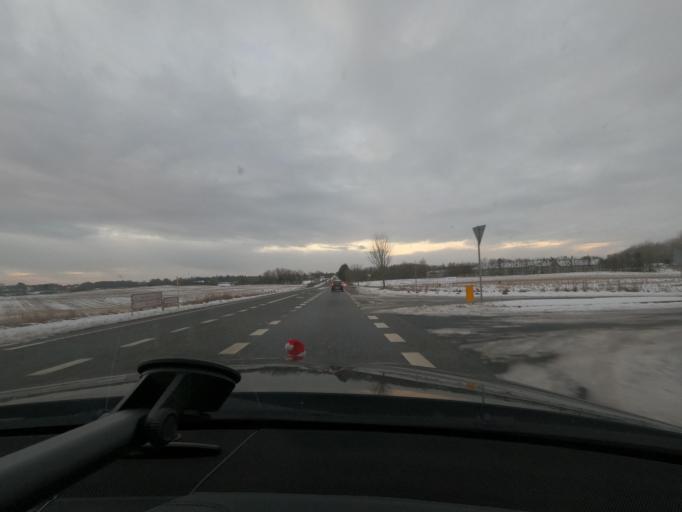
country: DK
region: South Denmark
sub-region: Aabenraa Kommune
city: Krusa
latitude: 54.8725
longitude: 9.4638
